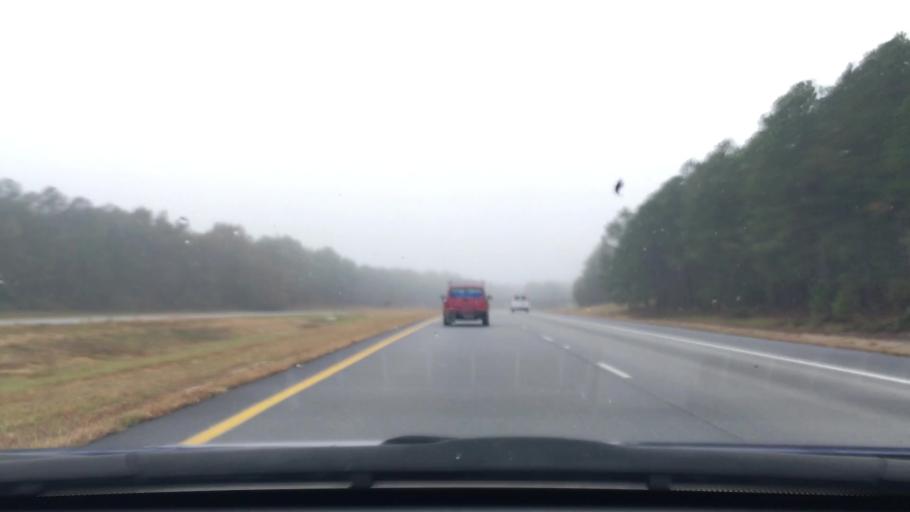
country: US
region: South Carolina
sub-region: Kershaw County
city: Camden
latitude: 34.2083
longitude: -80.4471
